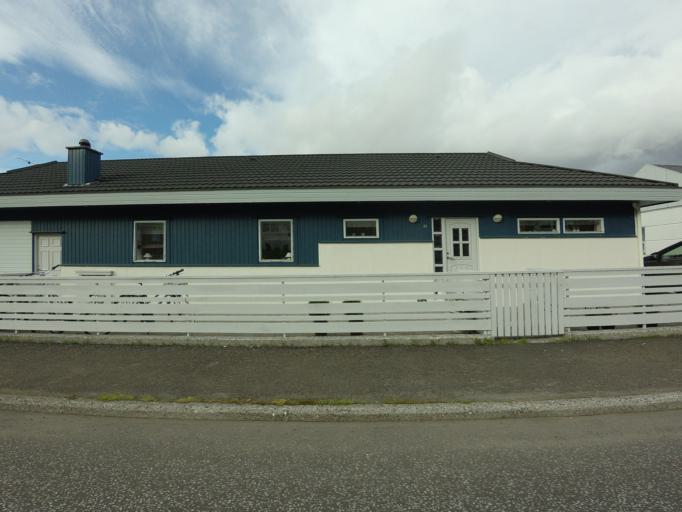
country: FO
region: Nordoyar
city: Klaksvik
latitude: 62.2205
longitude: -6.5808
